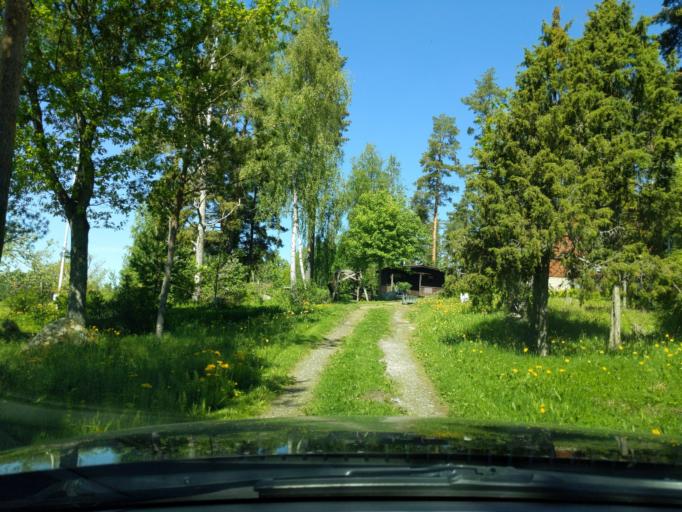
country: FI
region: Paijanne Tavastia
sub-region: Lahti
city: Lahti
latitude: 61.0575
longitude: 25.6739
